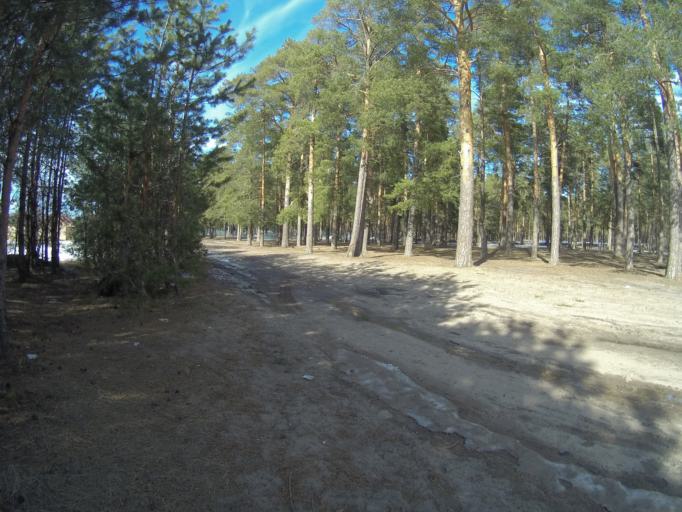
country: RU
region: Vladimir
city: Kommunar
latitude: 56.0984
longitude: 40.4376
